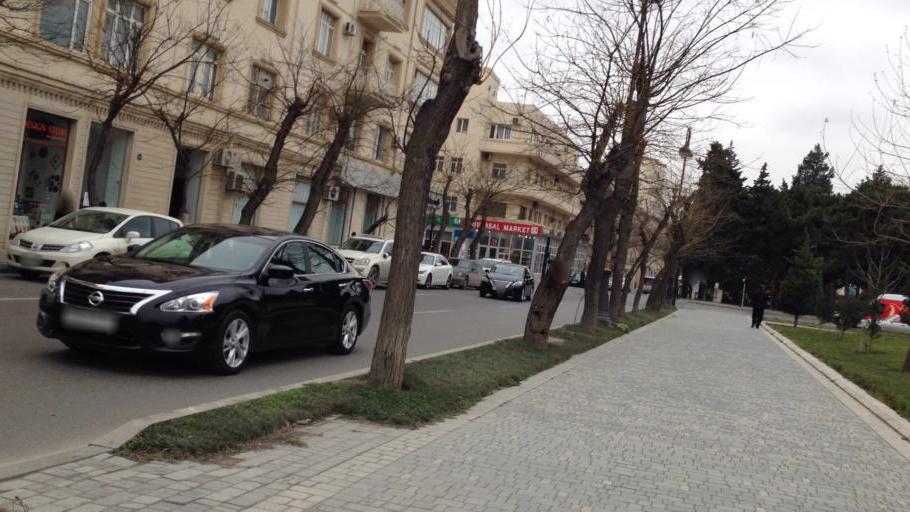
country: AZ
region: Baki
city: Baku
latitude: 40.3915
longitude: 49.8427
